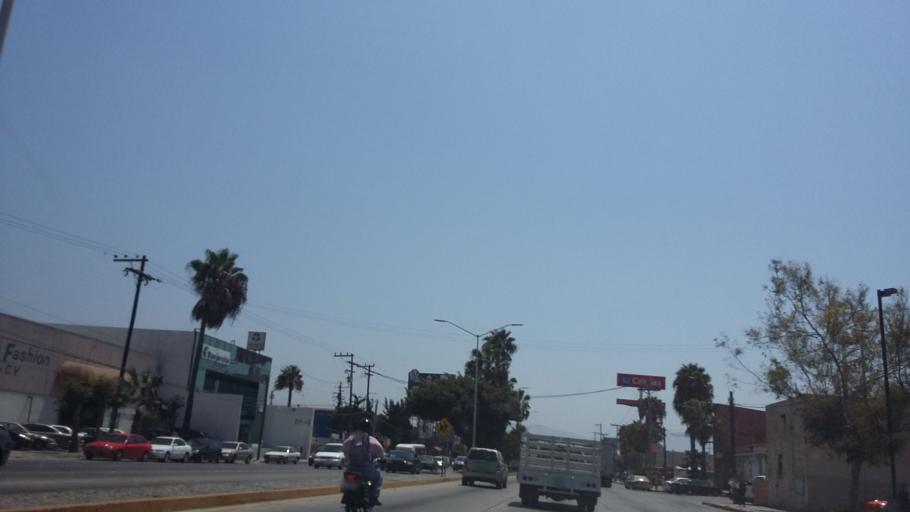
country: MX
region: Baja California
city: Ensenada
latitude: 31.8280
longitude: -116.6003
